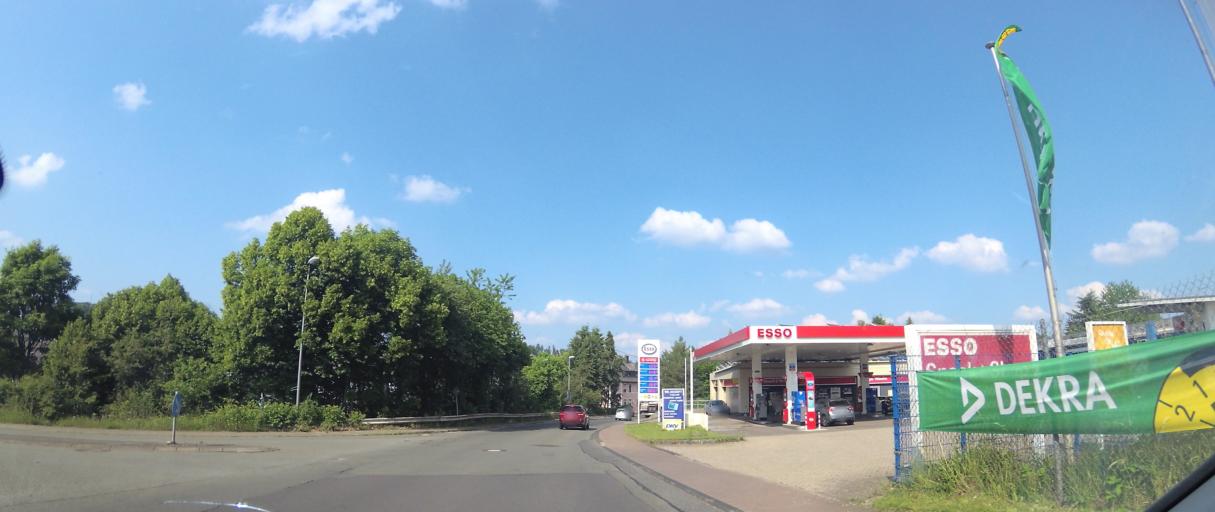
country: DE
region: Rheinland-Pfalz
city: Baumholder
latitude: 49.6114
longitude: 7.3323
